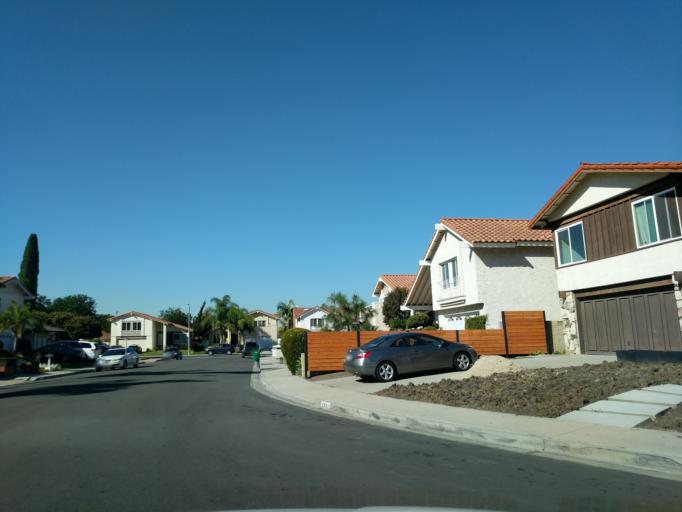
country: US
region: California
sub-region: Orange County
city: Irvine
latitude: 33.7033
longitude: -117.7899
